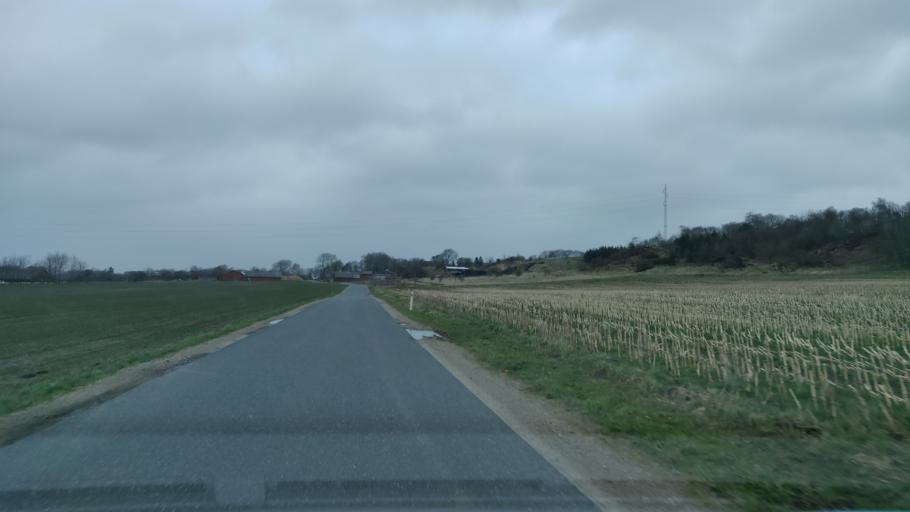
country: DK
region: Central Jutland
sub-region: Skive Kommune
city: Hojslev
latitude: 56.5502
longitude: 9.2415
